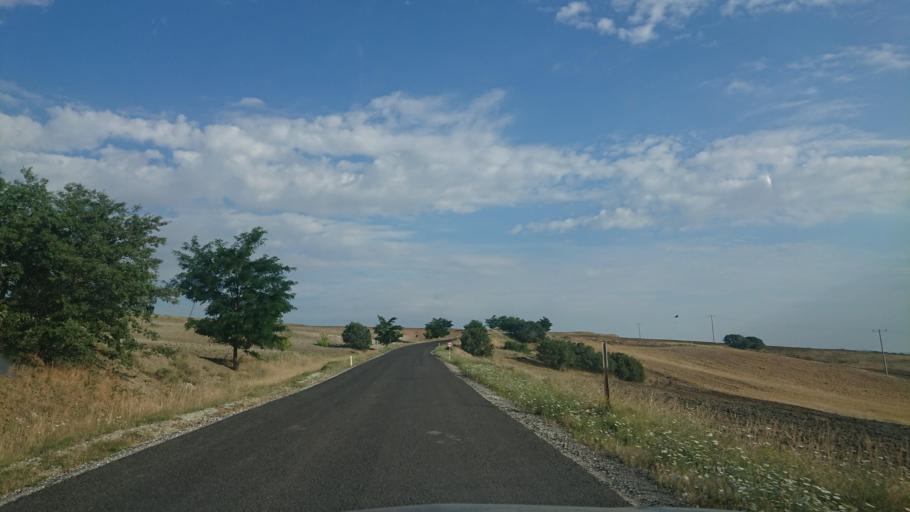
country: TR
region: Aksaray
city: Ortakoy
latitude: 38.8100
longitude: 34.0558
